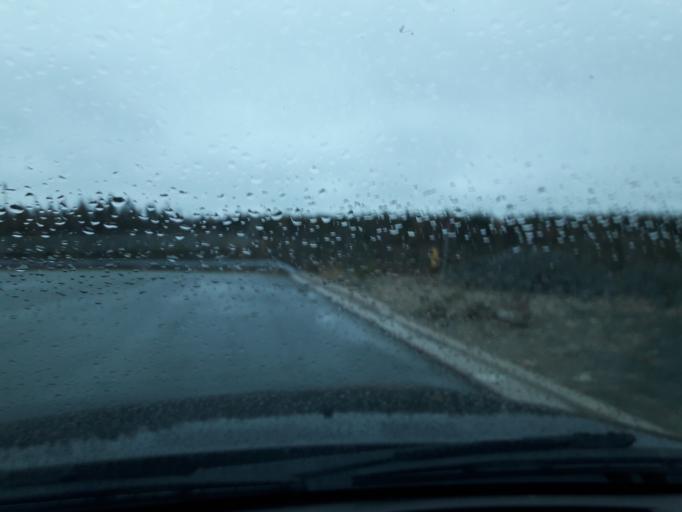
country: CA
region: Newfoundland and Labrador
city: Mount Pearl
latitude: 47.5585
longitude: -52.8039
